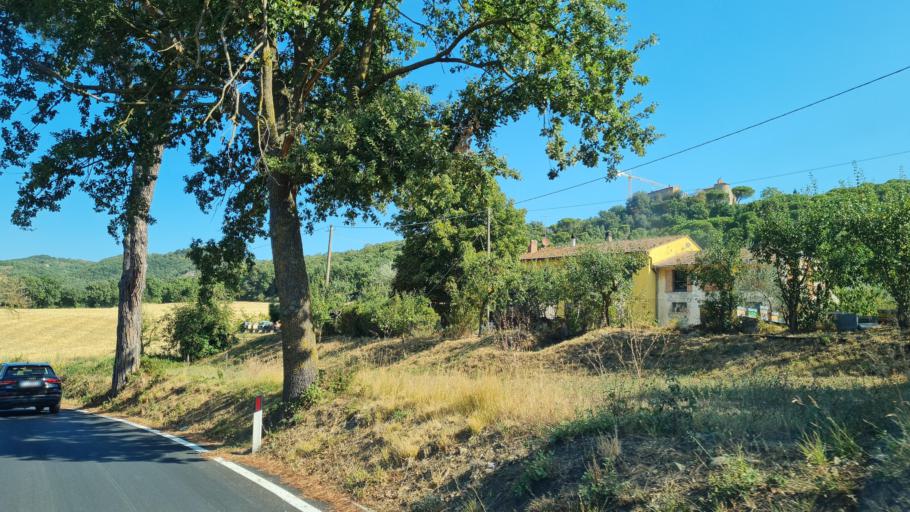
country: IT
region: Tuscany
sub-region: Provincia di Siena
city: Chianciano Terme
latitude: 43.0292
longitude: 11.7742
